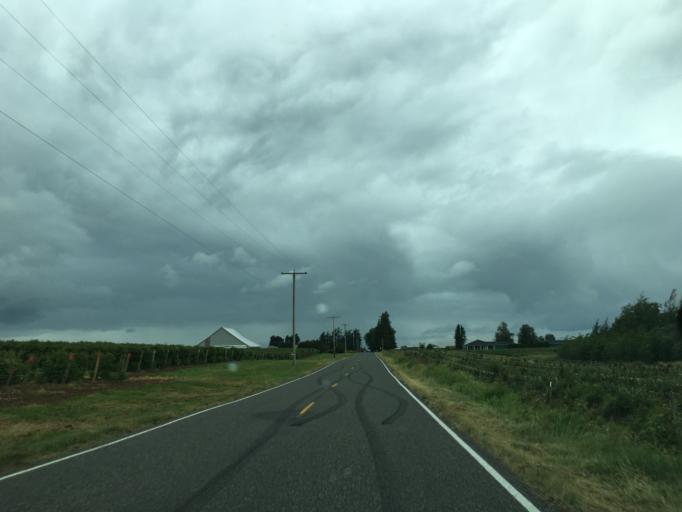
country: US
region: Washington
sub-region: Whatcom County
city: Everson
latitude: 48.9820
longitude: -122.3597
